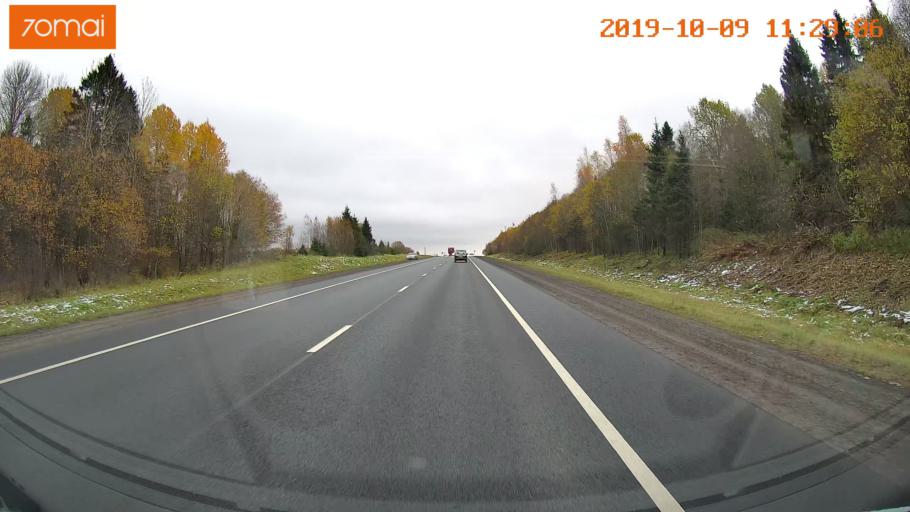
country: RU
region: Vologda
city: Vologda
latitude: 59.0643
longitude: 40.0483
